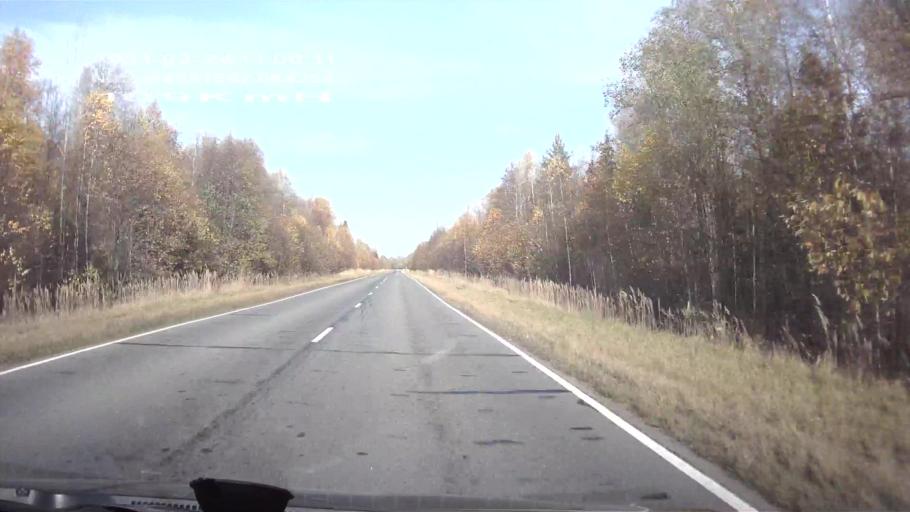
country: RU
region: Chuvashia
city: Buinsk
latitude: 55.1847
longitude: 47.0682
